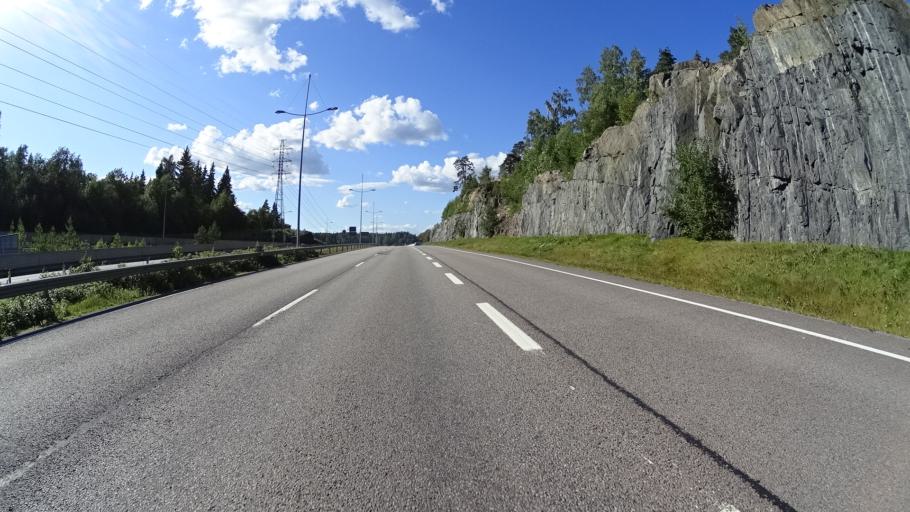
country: FI
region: Uusimaa
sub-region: Helsinki
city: Vantaa
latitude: 60.2469
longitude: 25.1434
